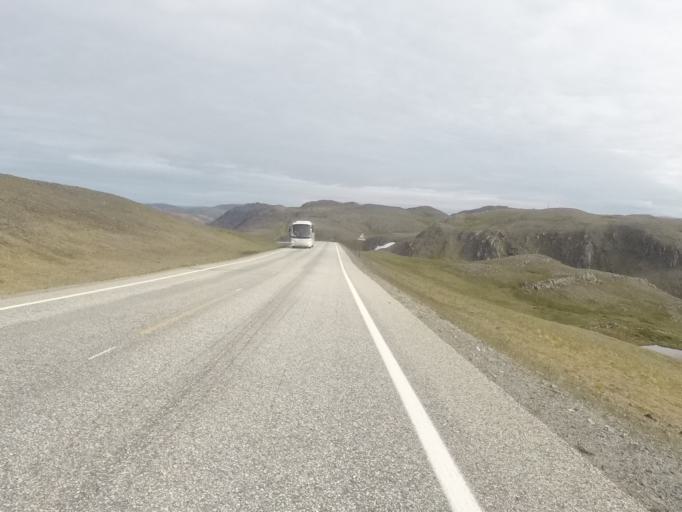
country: NO
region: Finnmark Fylke
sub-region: Nordkapp
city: Honningsvag
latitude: 71.0290
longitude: 25.8388
